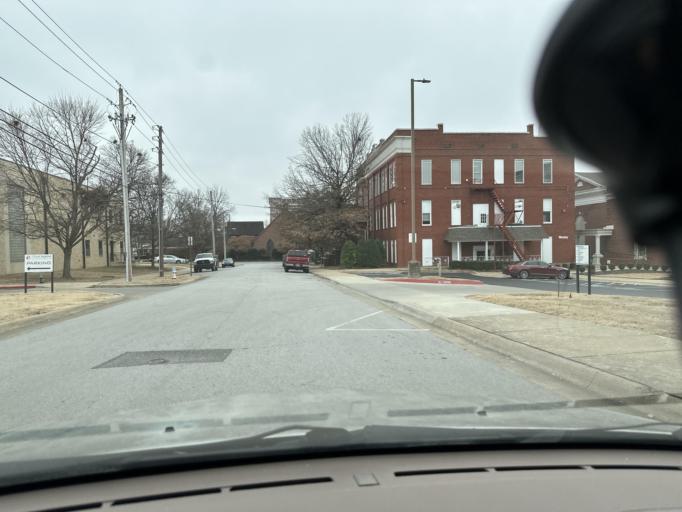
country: US
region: Arkansas
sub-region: Washington County
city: Fayetteville
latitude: 36.0673
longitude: -94.1590
